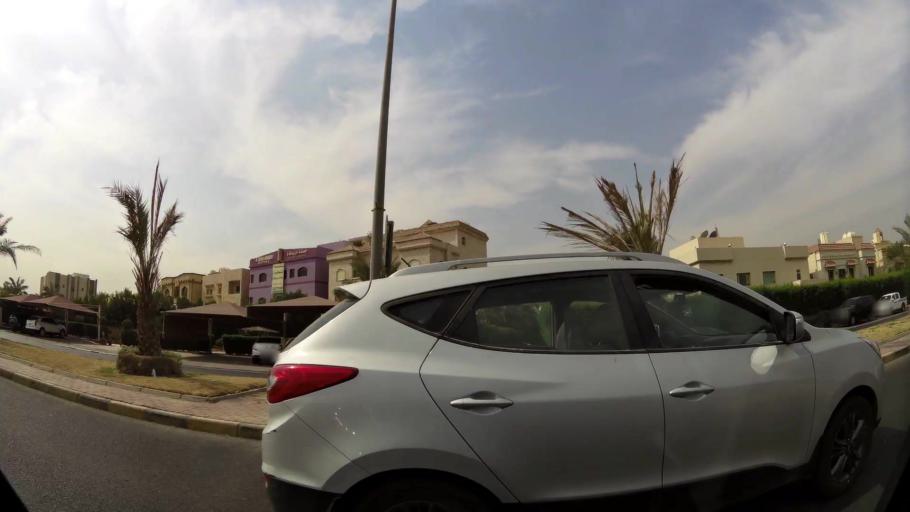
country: KW
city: Bayan
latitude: 29.2914
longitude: 48.0176
